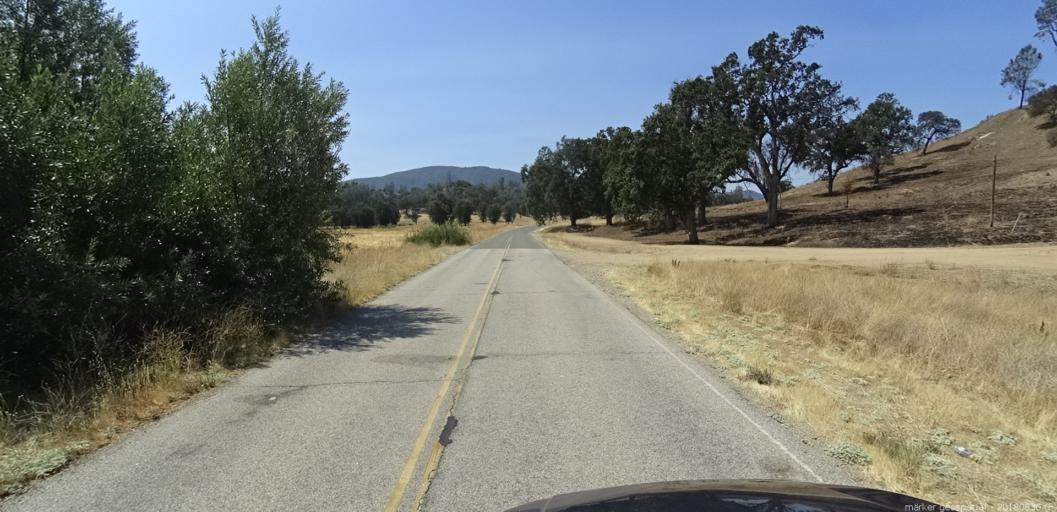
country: US
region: California
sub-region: Monterey County
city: King City
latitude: 35.9630
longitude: -121.2788
